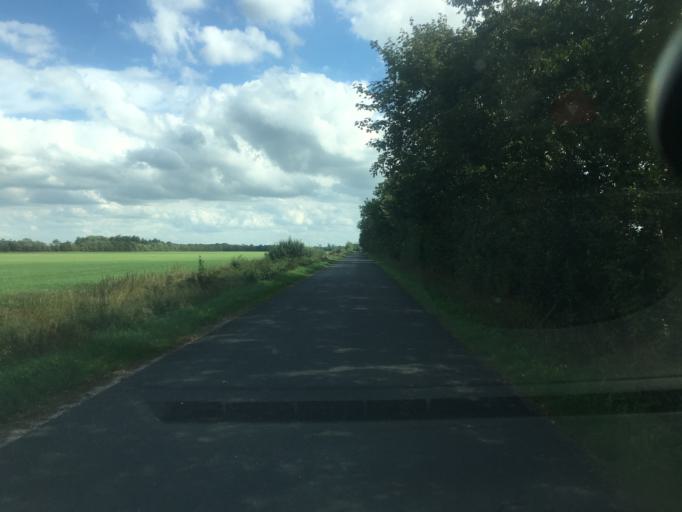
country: DK
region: South Denmark
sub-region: Tonder Kommune
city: Logumkloster
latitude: 55.0087
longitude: 9.0064
